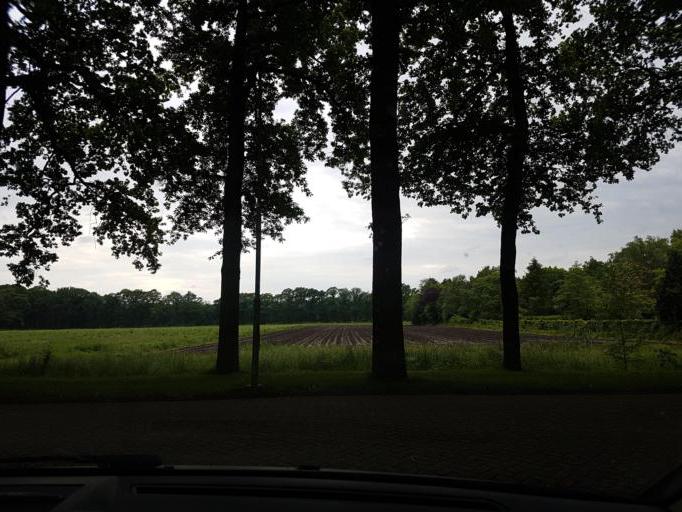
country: BE
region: Flanders
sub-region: Provincie Antwerpen
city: Merksplas
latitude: 51.3997
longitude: 4.8254
